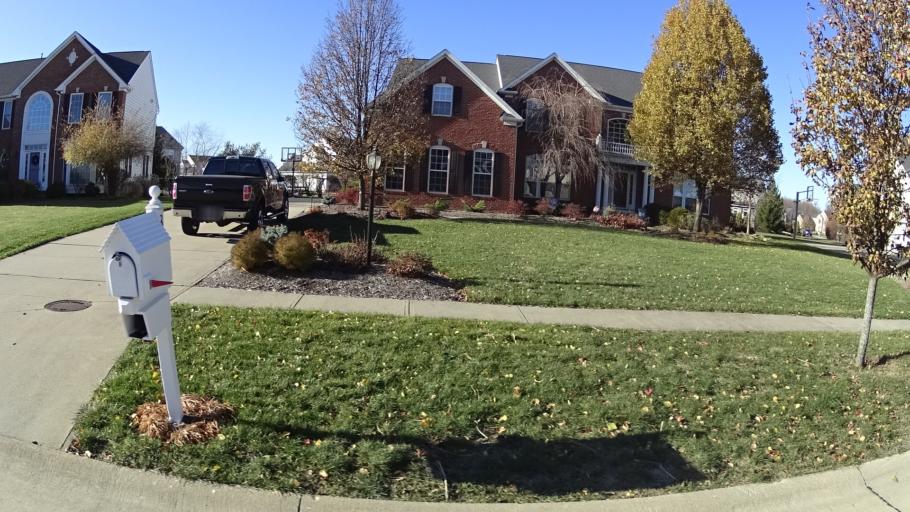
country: US
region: Ohio
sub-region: Lorain County
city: Avon Center
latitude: 41.4390
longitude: -81.9842
